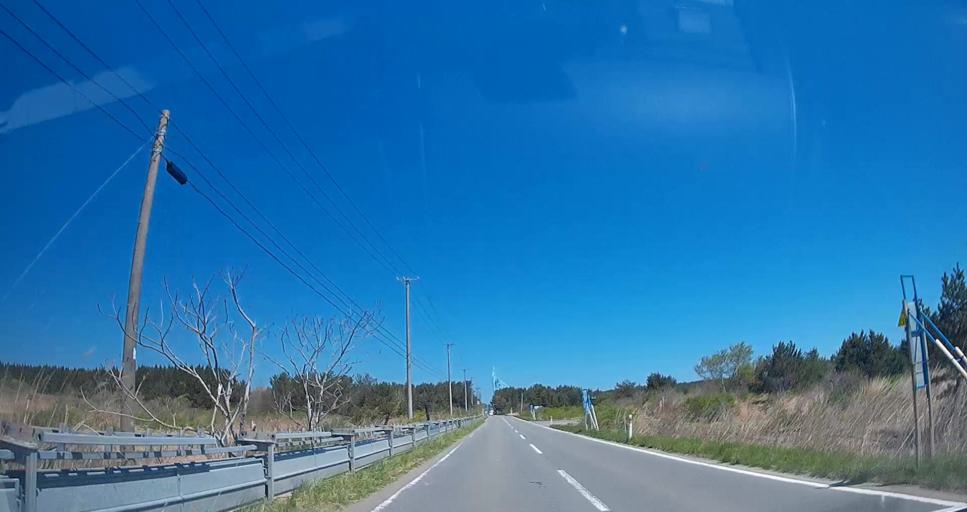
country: JP
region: Aomori
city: Misawa
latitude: 40.9330
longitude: 141.3749
